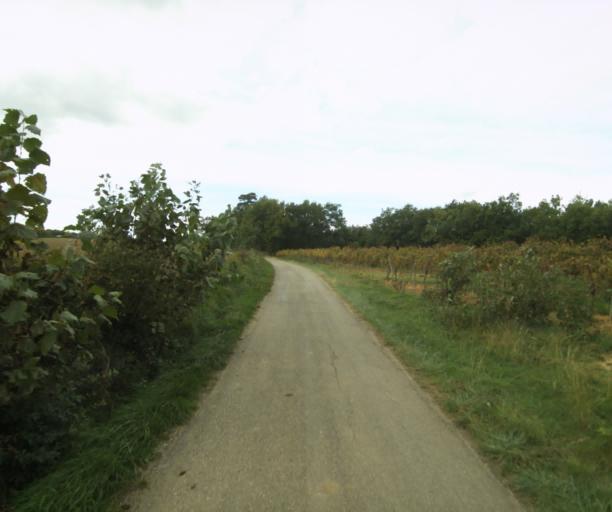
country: FR
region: Midi-Pyrenees
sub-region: Departement du Gers
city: Gondrin
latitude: 43.8665
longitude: 0.2559
